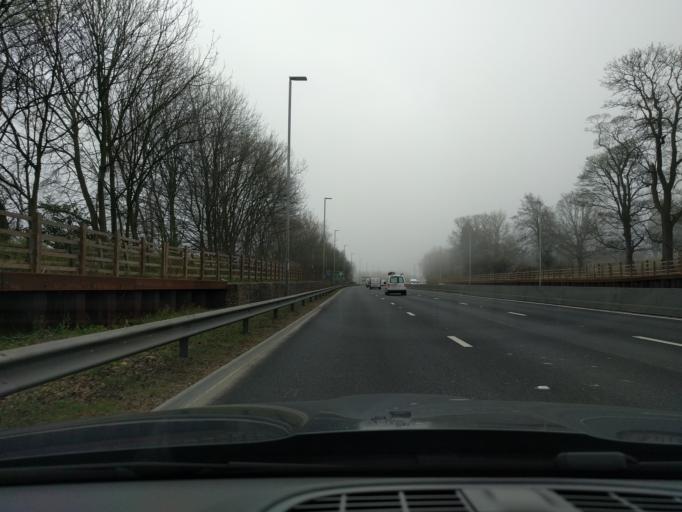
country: GB
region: England
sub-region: Gateshead
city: Lamesley
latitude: 54.9361
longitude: -1.6289
